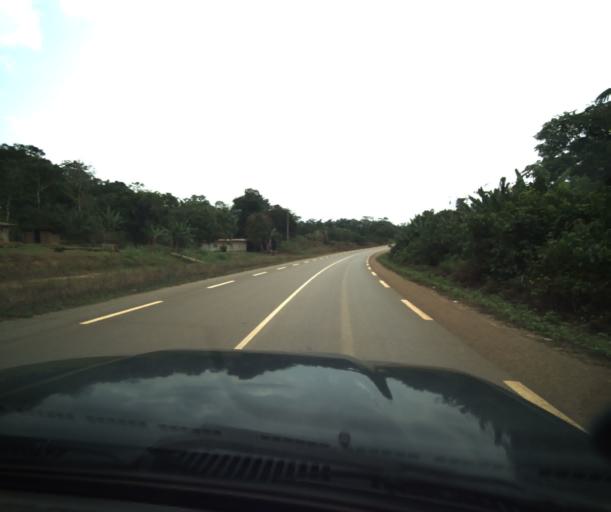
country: CM
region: Centre
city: Akono
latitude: 3.6115
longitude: 11.3145
